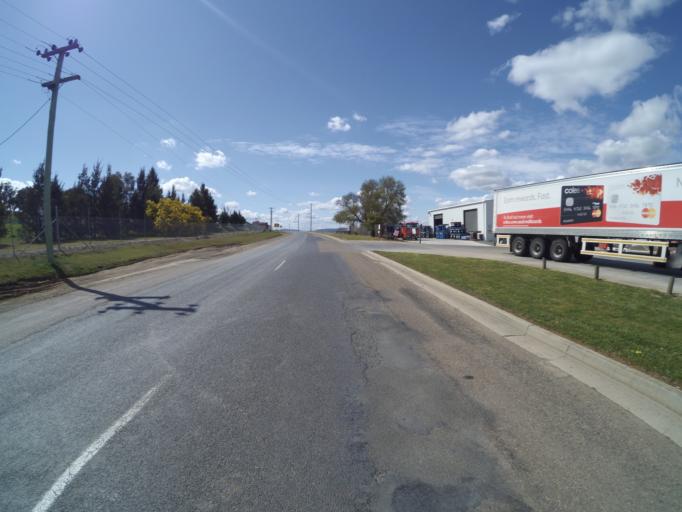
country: AU
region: New South Wales
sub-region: Goulburn Mulwaree
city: Goulburn
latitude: -34.7742
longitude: 149.7084
